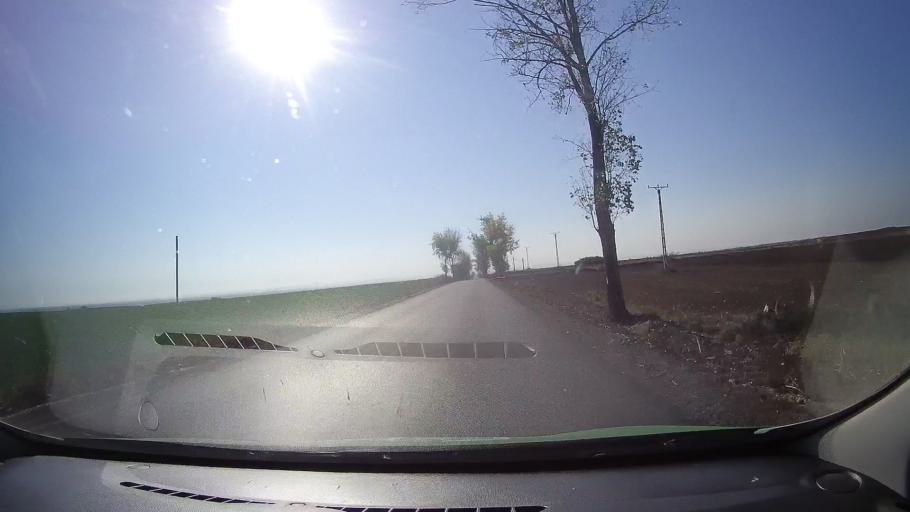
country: RO
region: Satu Mare
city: Carei
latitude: 47.6544
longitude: 22.4611
